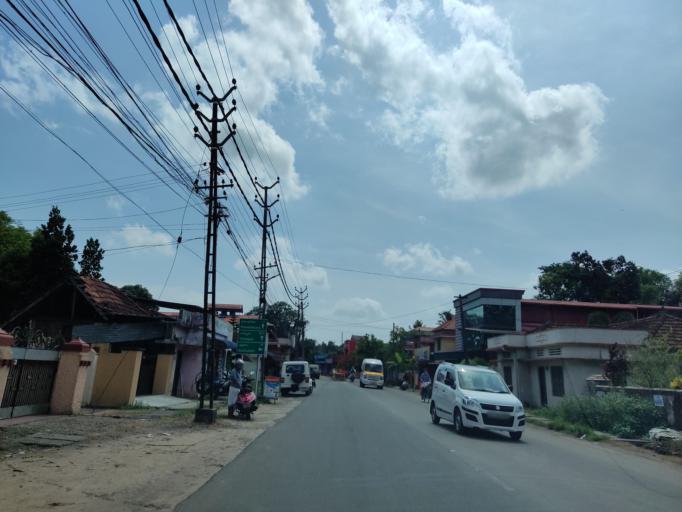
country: IN
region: Kerala
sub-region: Alappuzha
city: Mavelikara
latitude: 9.2547
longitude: 76.5497
